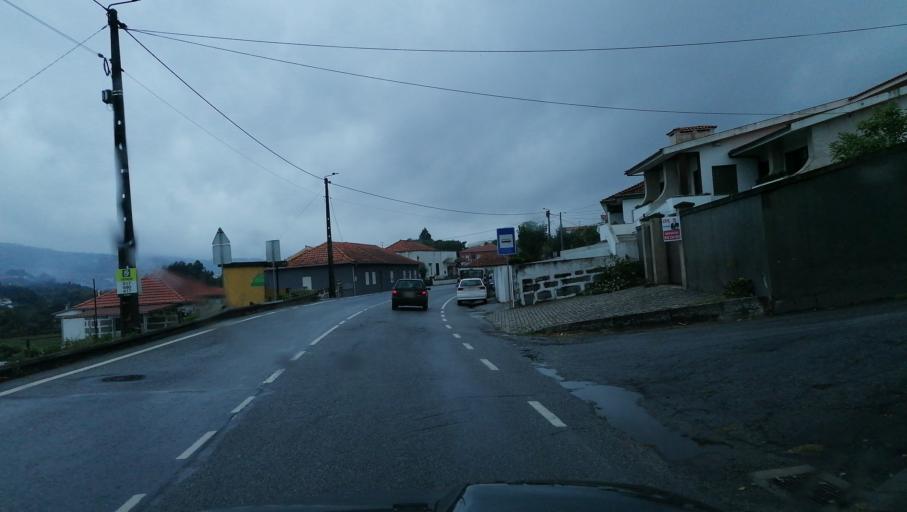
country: PT
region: Braga
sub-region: Guimaraes
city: Lordelo
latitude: 41.3690
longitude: -8.3824
